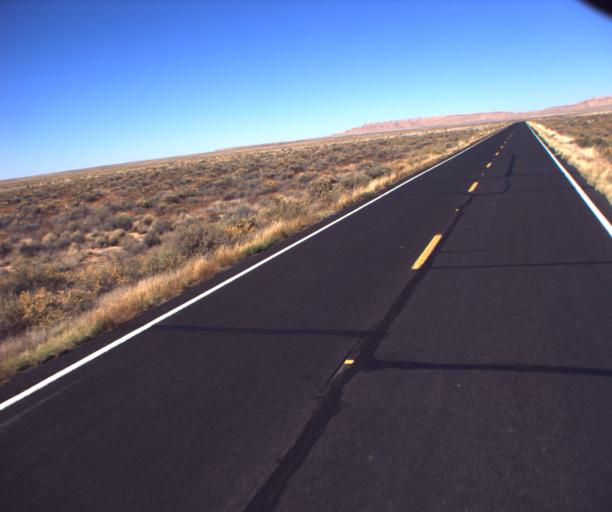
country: US
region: Arizona
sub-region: Navajo County
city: First Mesa
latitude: 35.7238
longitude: -110.5161
